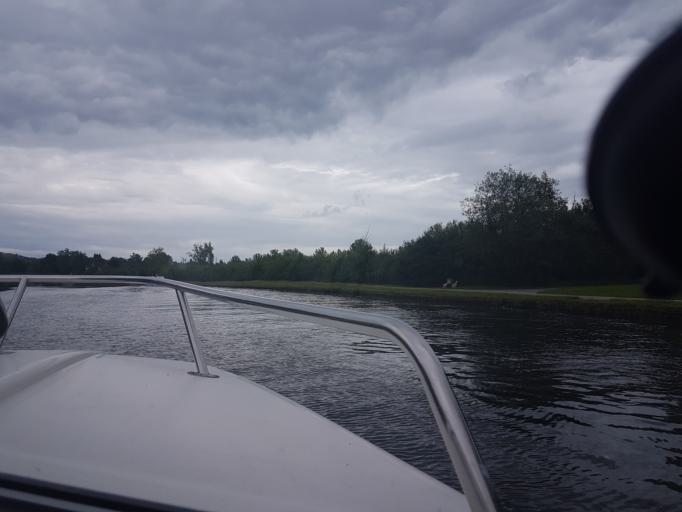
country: FR
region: Bourgogne
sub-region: Departement de l'Yonne
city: Champs-sur-Yonne
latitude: 47.7261
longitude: 3.6088
